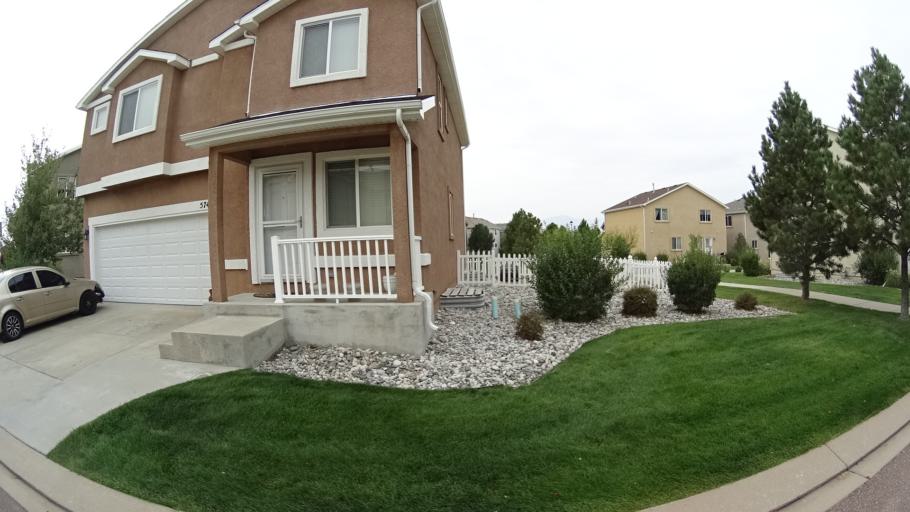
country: US
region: Colorado
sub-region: El Paso County
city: Cimarron Hills
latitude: 38.9169
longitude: -104.6847
